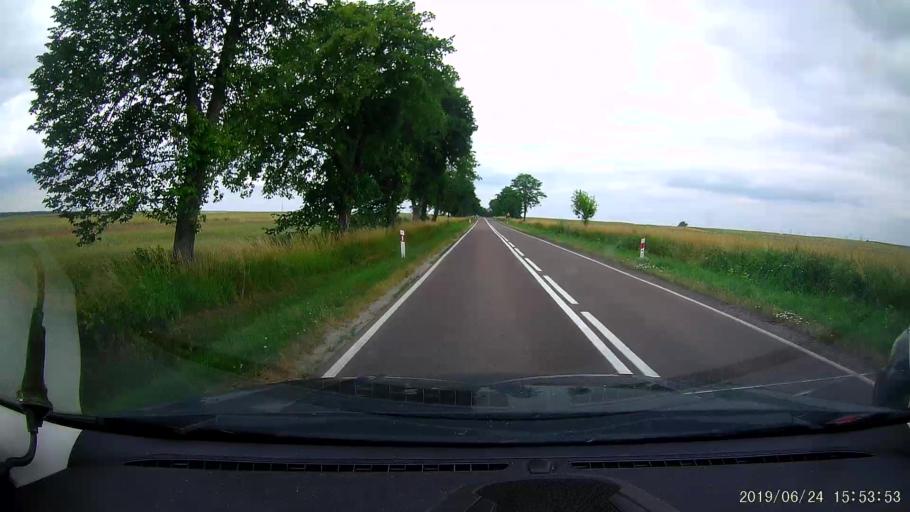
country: PL
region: Subcarpathian Voivodeship
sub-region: Powiat lubaczowski
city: Cieszanow
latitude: 50.2104
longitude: 23.1113
